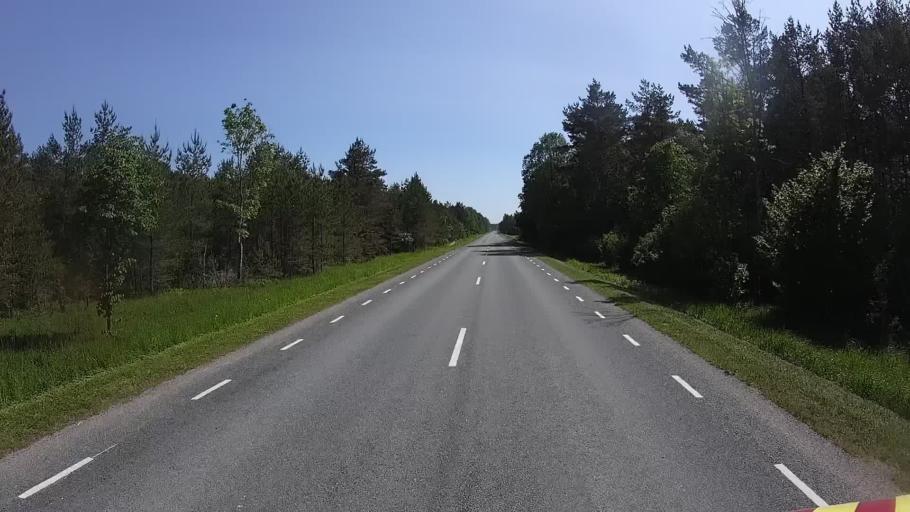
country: EE
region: Saare
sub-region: Kuressaare linn
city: Kuressaare
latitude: 58.3712
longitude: 22.4355
